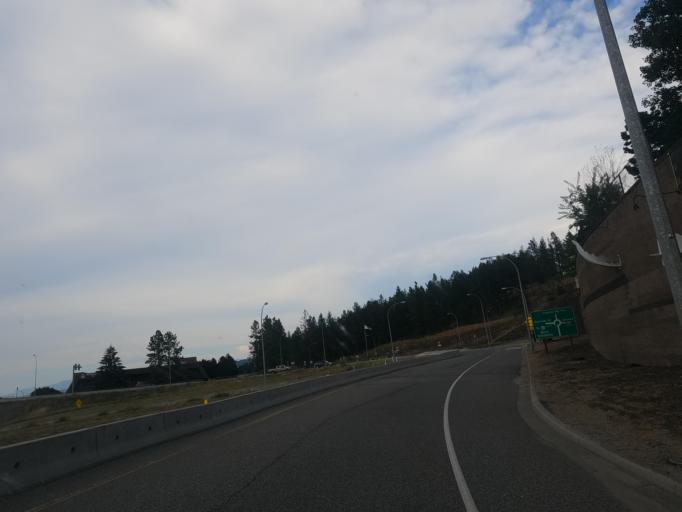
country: CA
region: British Columbia
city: Kelowna
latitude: 49.8808
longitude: -119.5356
